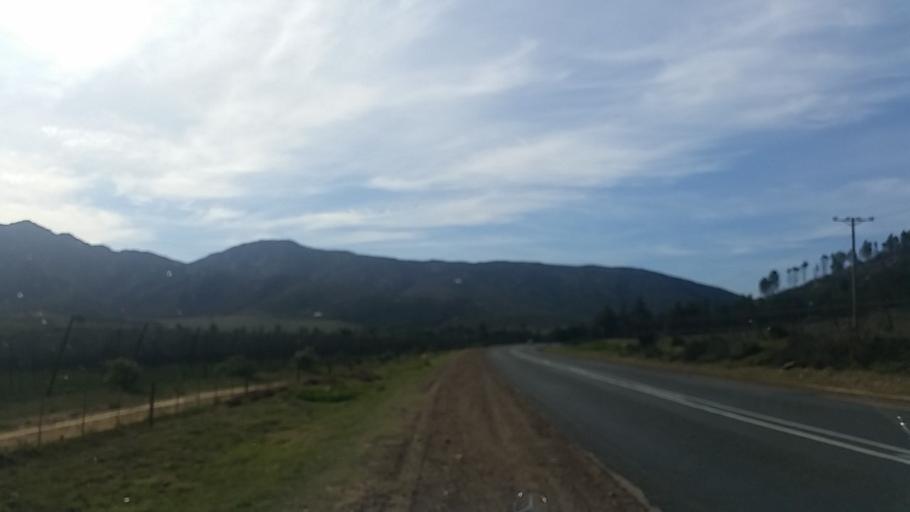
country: ZA
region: Western Cape
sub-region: Eden District Municipality
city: George
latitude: -33.8473
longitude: 22.3530
